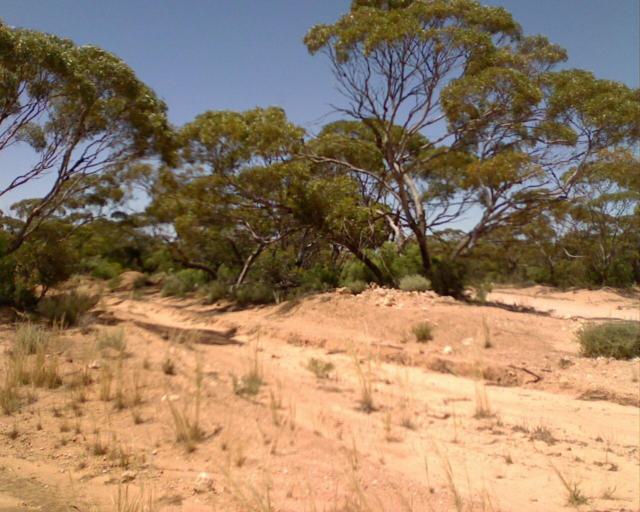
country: AU
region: South Australia
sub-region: Kimba
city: Caralue
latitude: -32.9434
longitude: 135.2709
